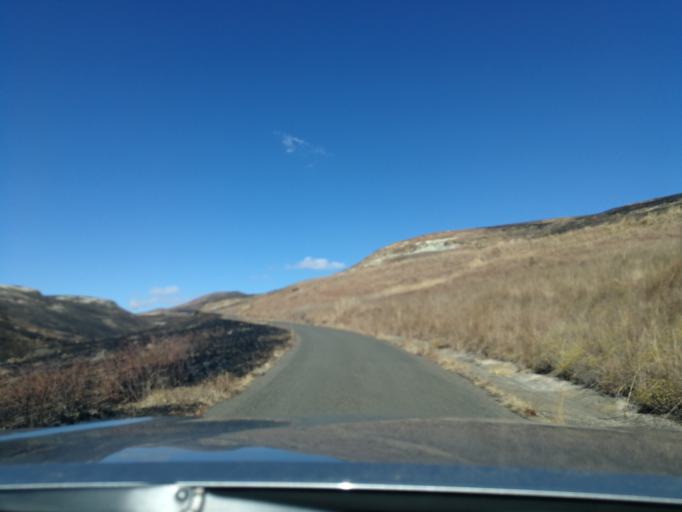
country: ZA
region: Orange Free State
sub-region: Thabo Mofutsanyana District Municipality
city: Phuthaditjhaba
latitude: -28.5108
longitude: 28.6251
